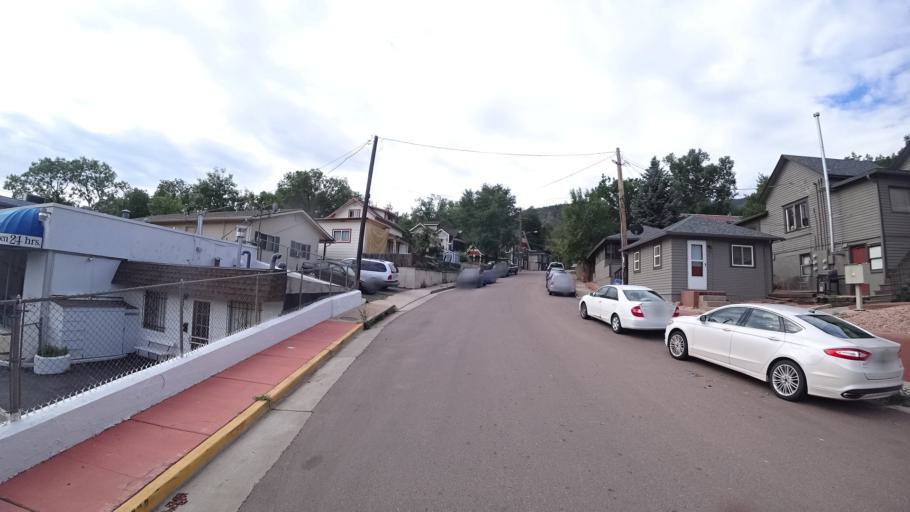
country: US
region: Colorado
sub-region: El Paso County
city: Manitou Springs
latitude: 38.8574
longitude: -104.9123
